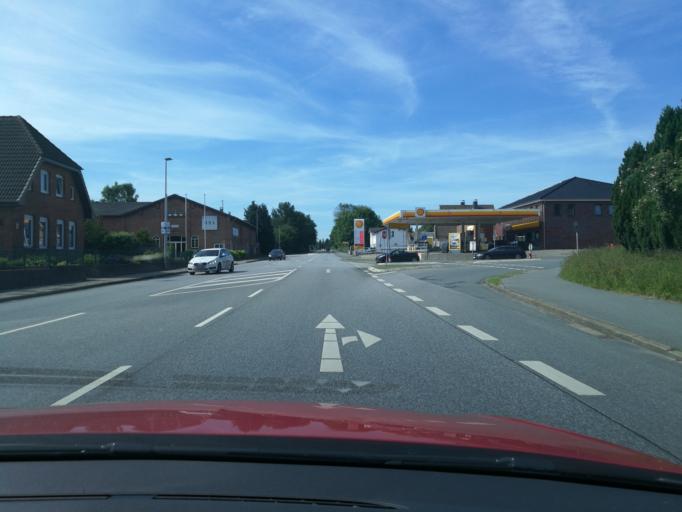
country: DE
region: Schleswig-Holstein
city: Elmenhorst
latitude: 53.7656
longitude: 10.2638
